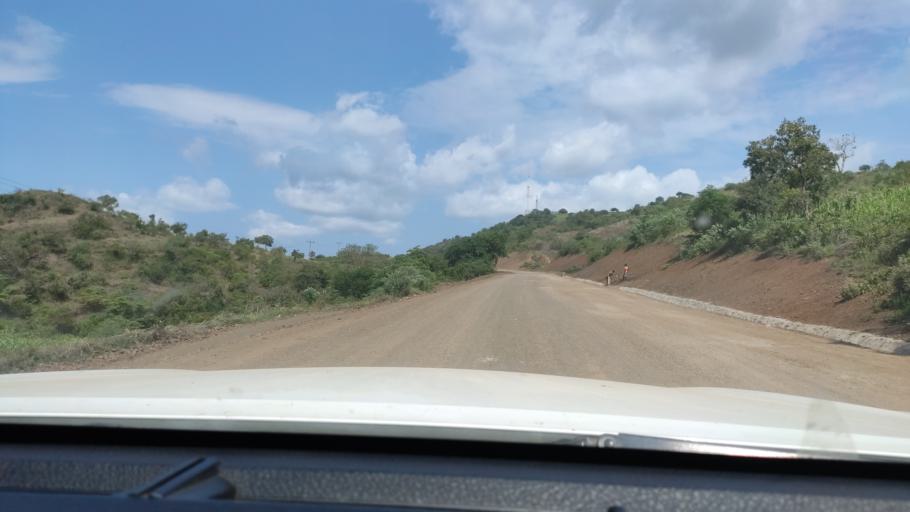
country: ET
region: Southern Nations, Nationalities, and People's Region
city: Felege Neway
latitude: 6.3907
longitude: 37.0659
